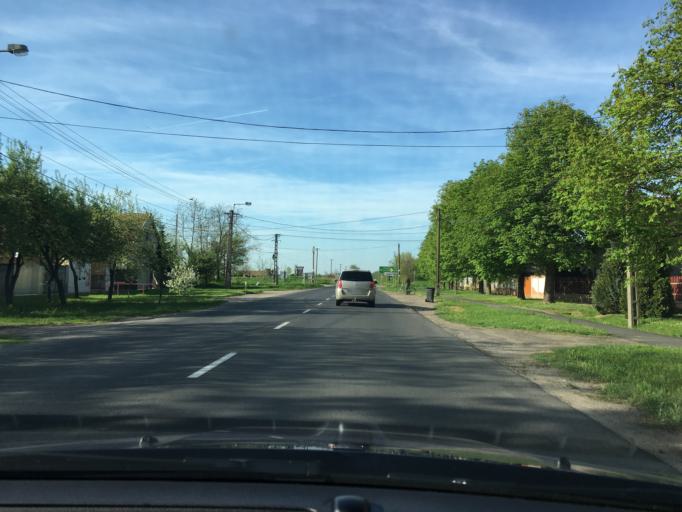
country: HU
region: Bekes
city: Mezobereny
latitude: 46.8410
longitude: 21.0278
